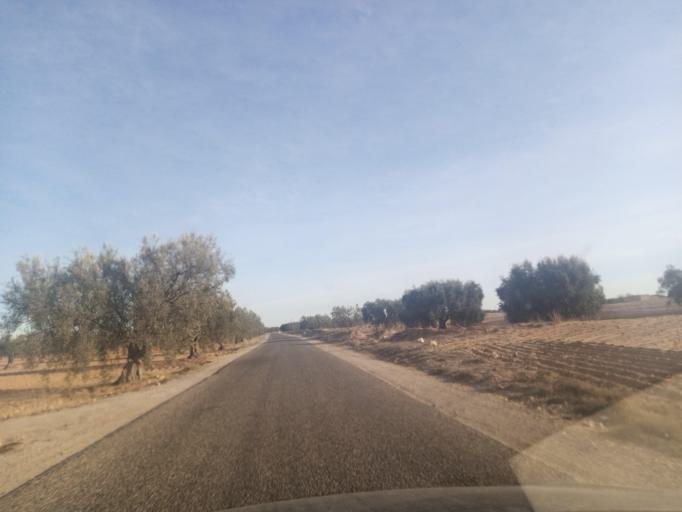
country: TN
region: Safaqis
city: Bi'r `Ali Bin Khalifah
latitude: 34.8898
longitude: 10.1781
